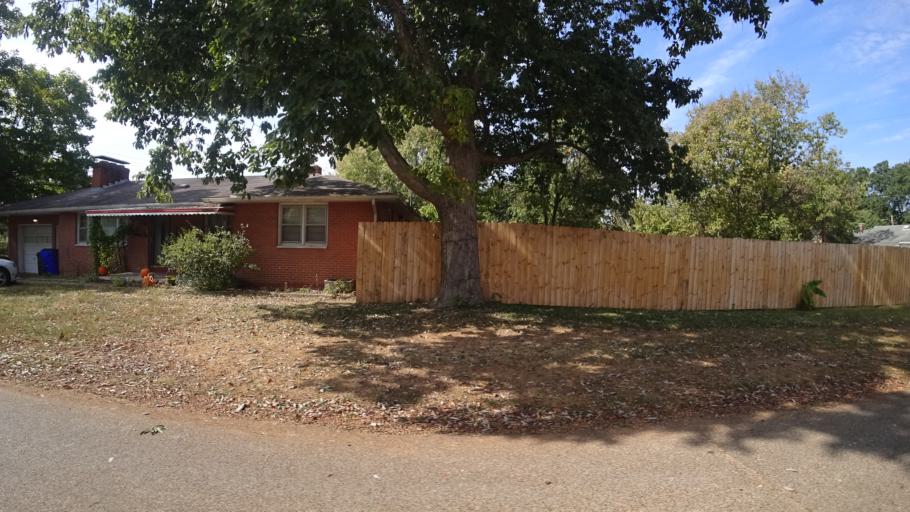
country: US
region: Ohio
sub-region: Butler County
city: Fairfield
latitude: 39.3592
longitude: -84.5517
